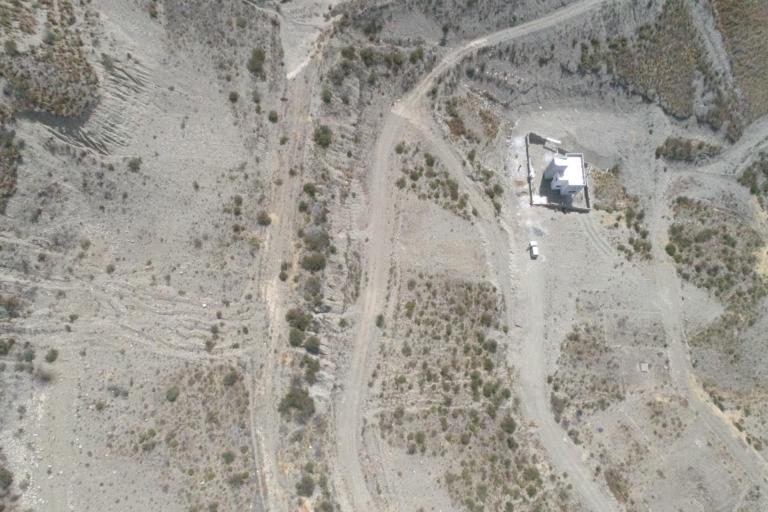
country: BO
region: La Paz
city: La Paz
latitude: -16.4748
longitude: -68.0983
